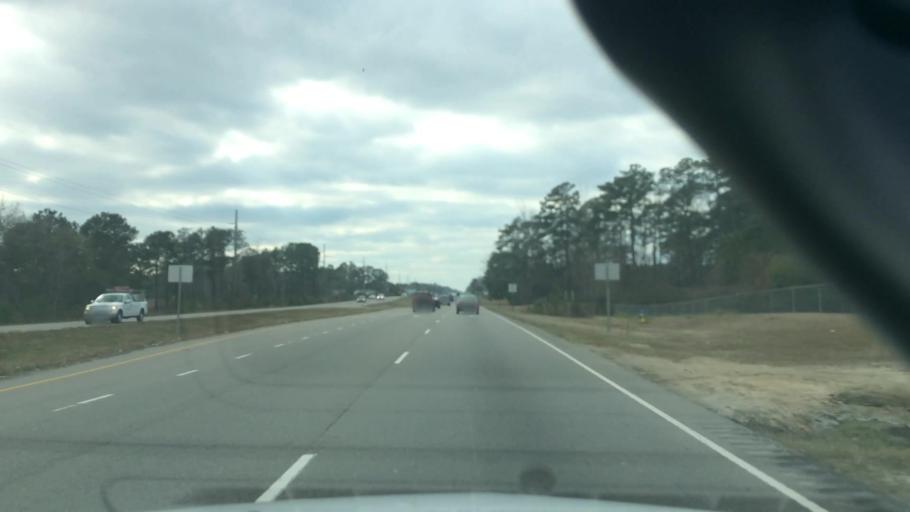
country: US
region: North Carolina
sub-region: Brunswick County
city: Shallotte
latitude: 34.0162
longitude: -78.2765
